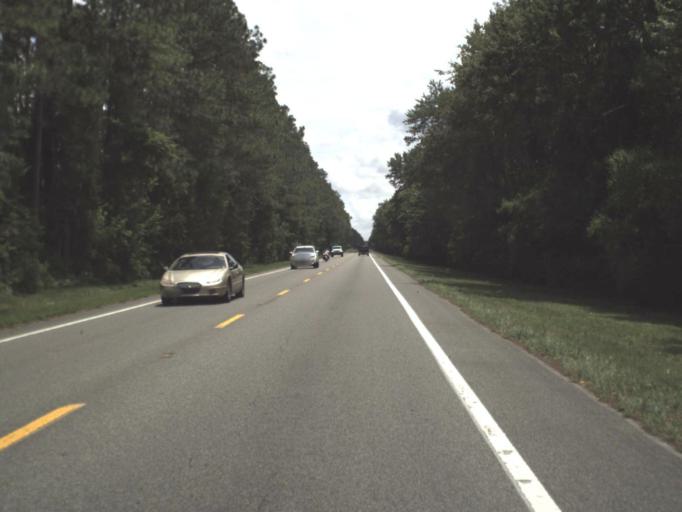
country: US
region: Florida
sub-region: Nassau County
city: Yulee
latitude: 30.6783
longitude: -81.6466
